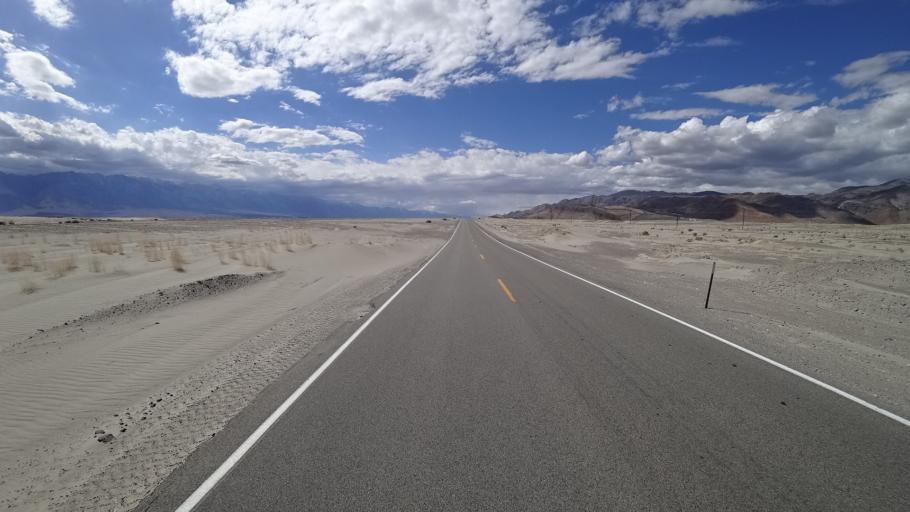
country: US
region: California
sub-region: Inyo County
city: Lone Pine
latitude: 36.4986
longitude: -117.8809
